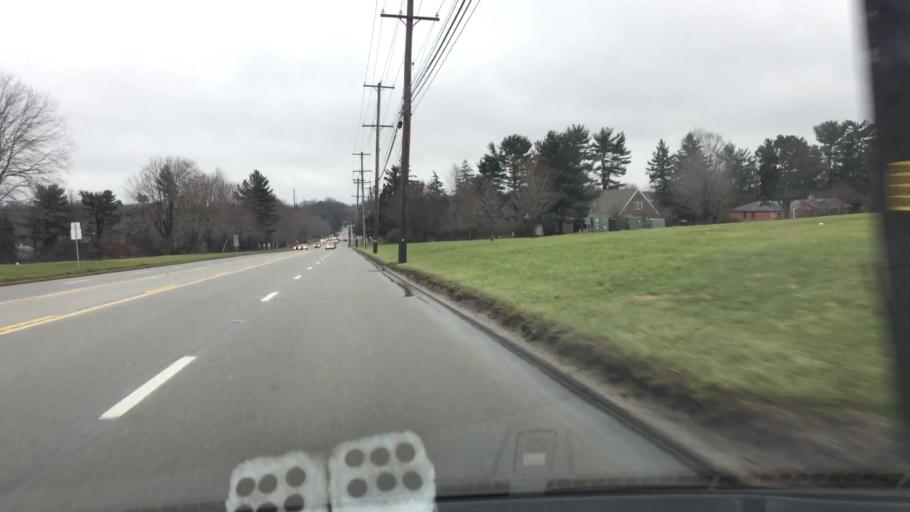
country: US
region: Pennsylvania
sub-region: Delaware County
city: Lima
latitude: 39.9116
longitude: -75.4217
